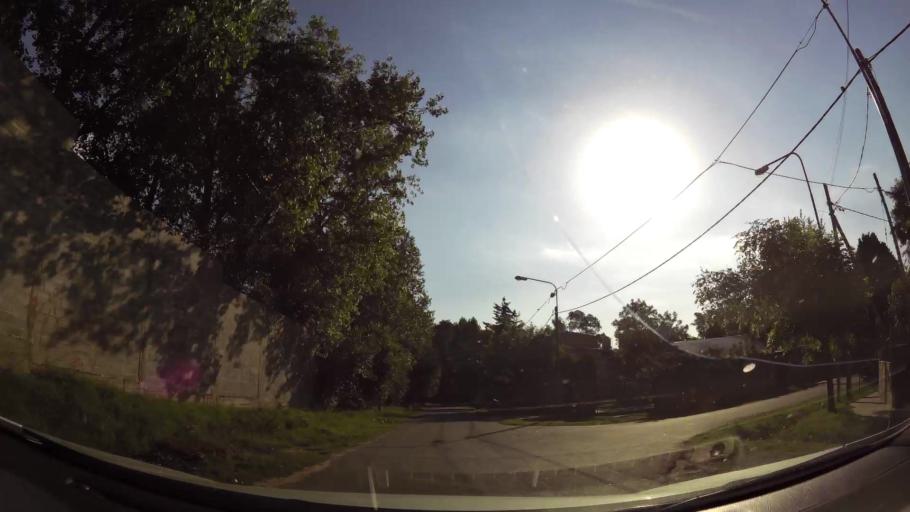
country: AR
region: Buenos Aires
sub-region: Partido de Tigre
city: Tigre
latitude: -34.4768
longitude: -58.6460
